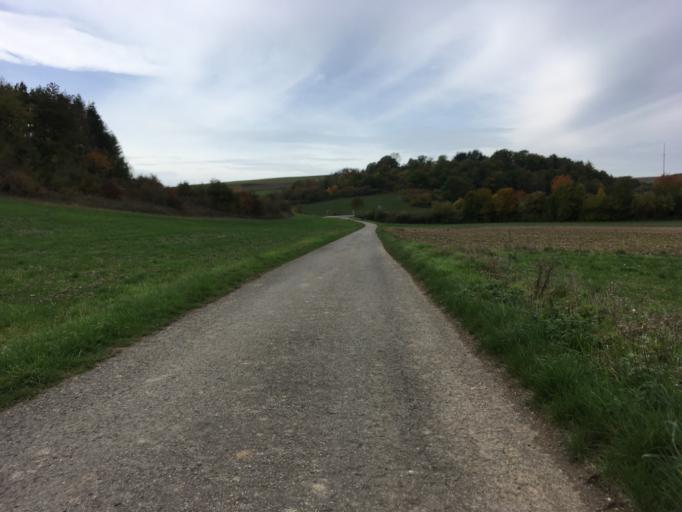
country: DE
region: Baden-Wuerttemberg
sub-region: Karlsruhe Region
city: Rosenberg
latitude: 49.5104
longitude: 9.4412
